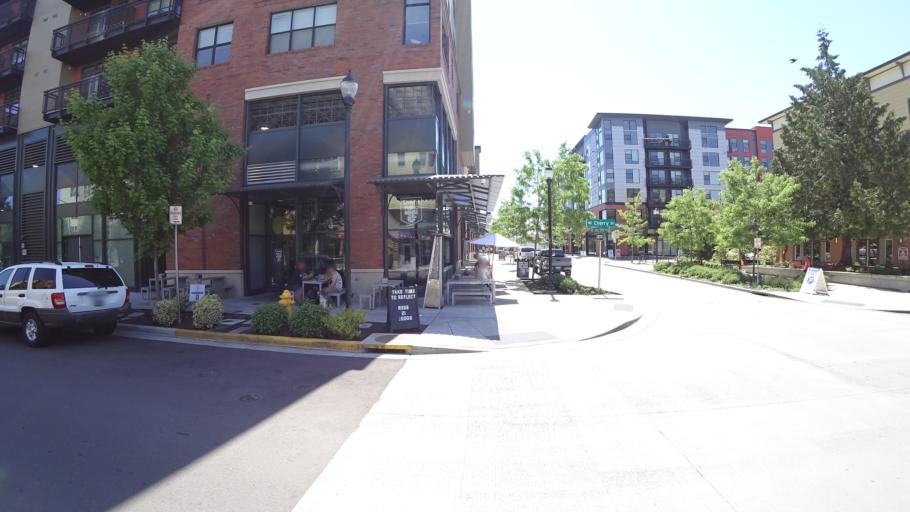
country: US
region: Oregon
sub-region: Washington County
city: Rockcreek
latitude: 45.5314
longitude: -122.9167
